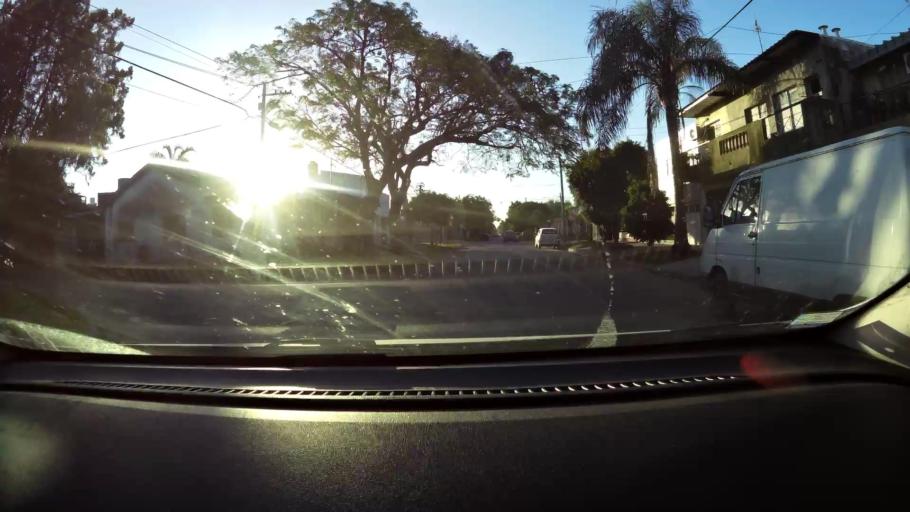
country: AR
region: Santa Fe
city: Santa Fe de la Vera Cruz
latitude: -31.5991
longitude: -60.6882
